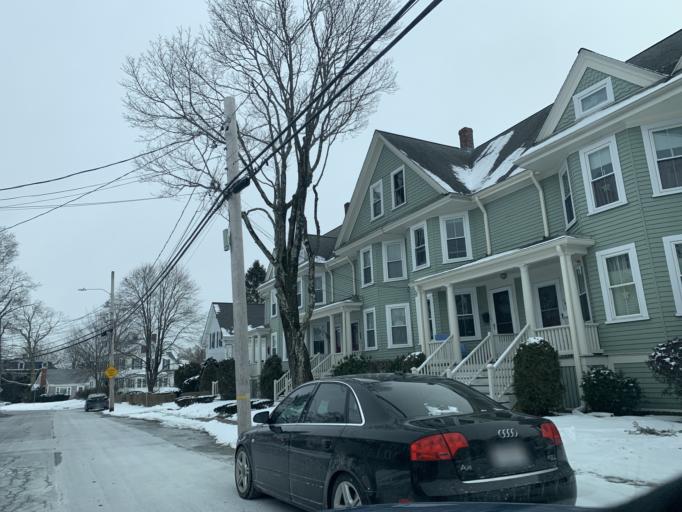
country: US
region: Massachusetts
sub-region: Norfolk County
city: Norwood
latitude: 42.1947
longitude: -71.2059
